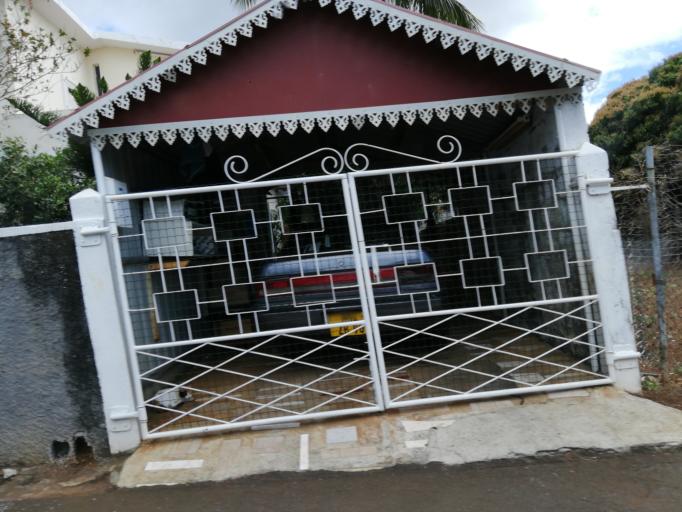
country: MU
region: Moka
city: Pailles
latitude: -20.2061
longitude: 57.4714
